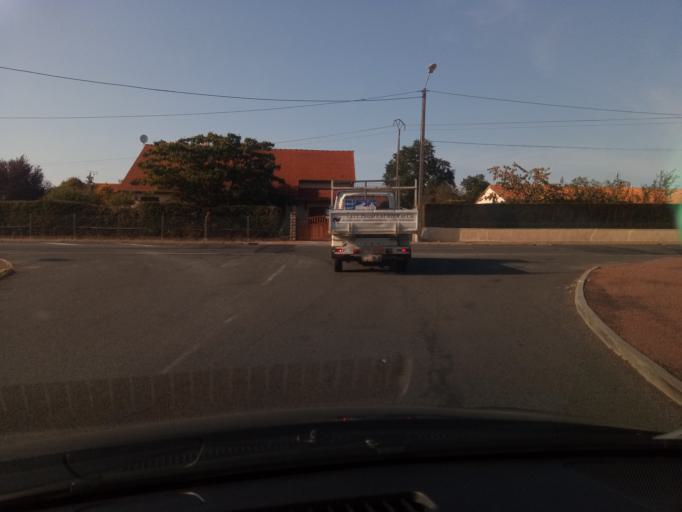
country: FR
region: Poitou-Charentes
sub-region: Departement de la Vienne
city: Montmorillon
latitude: 46.4307
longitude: 0.8860
